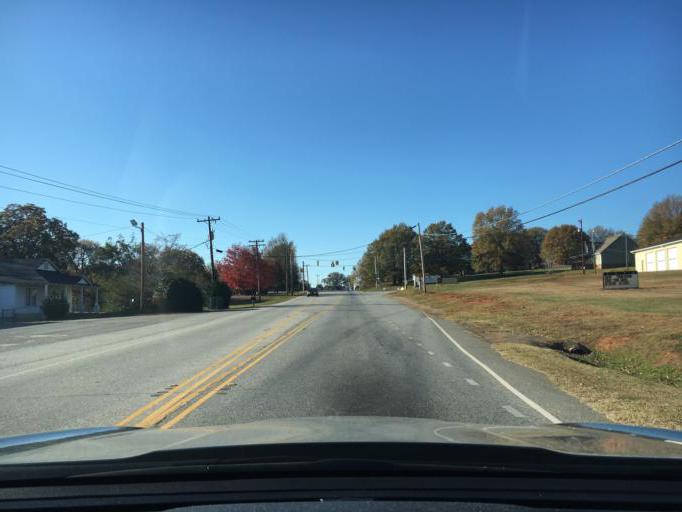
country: US
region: South Carolina
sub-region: Spartanburg County
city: Inman Mills
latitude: 35.0542
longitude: -82.1147
